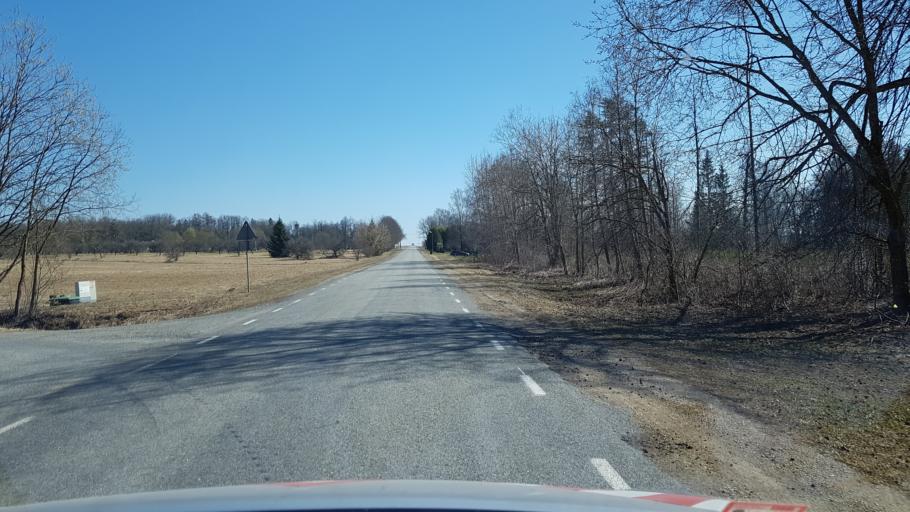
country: EE
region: Laeaene-Virumaa
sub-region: Vaeike-Maarja vald
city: Vaike-Maarja
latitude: 59.1177
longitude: 26.3244
